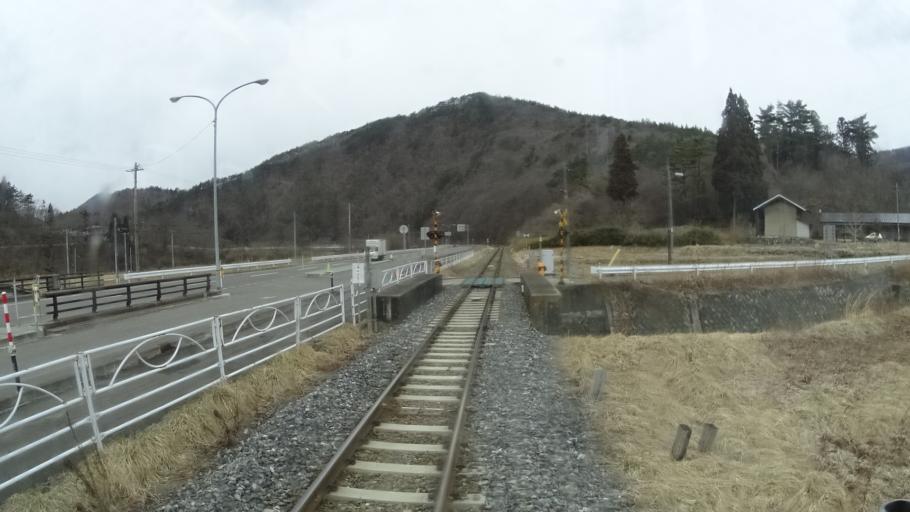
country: JP
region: Iwate
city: Tono
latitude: 39.3011
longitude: 141.3947
